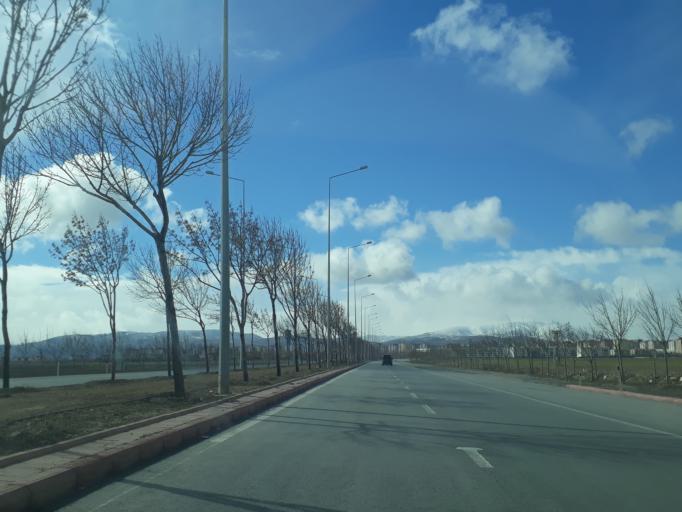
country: TR
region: Konya
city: Asagipinarbasi
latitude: 38.0048
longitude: 32.5514
